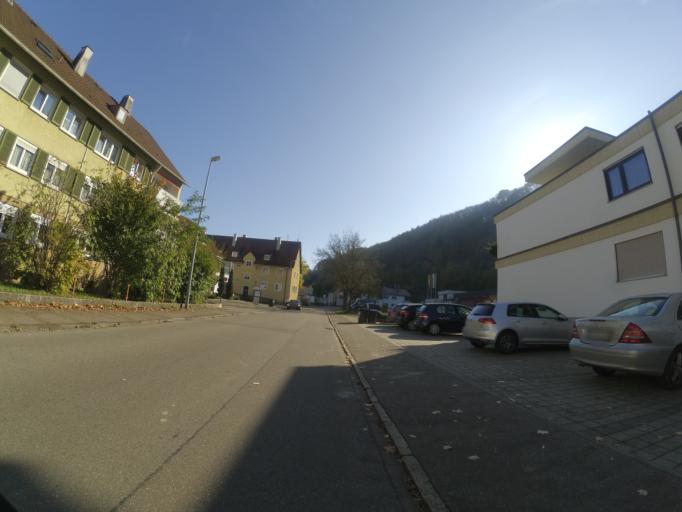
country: DE
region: Baden-Wuerttemberg
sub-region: Tuebingen Region
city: Blaubeuren
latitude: 48.4098
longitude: 9.7843
